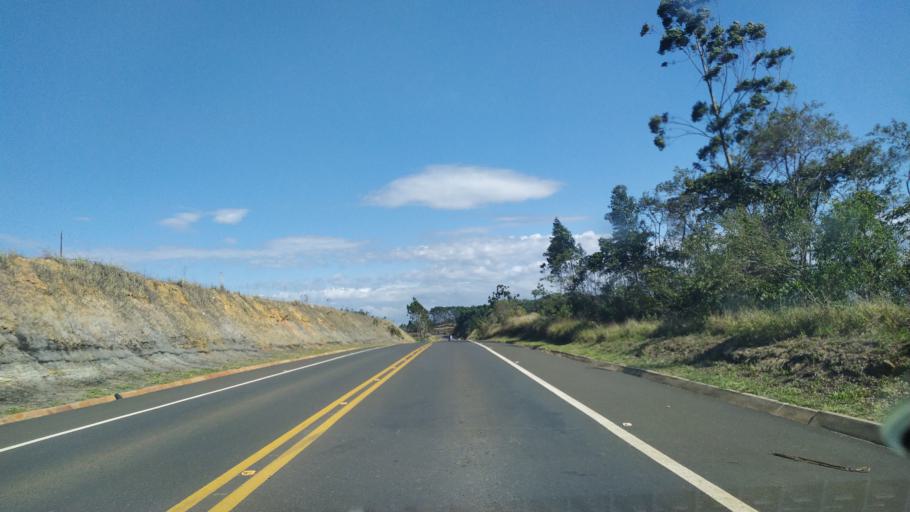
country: BR
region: Parana
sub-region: Ortigueira
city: Ortigueira
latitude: -24.2856
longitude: -50.8124
